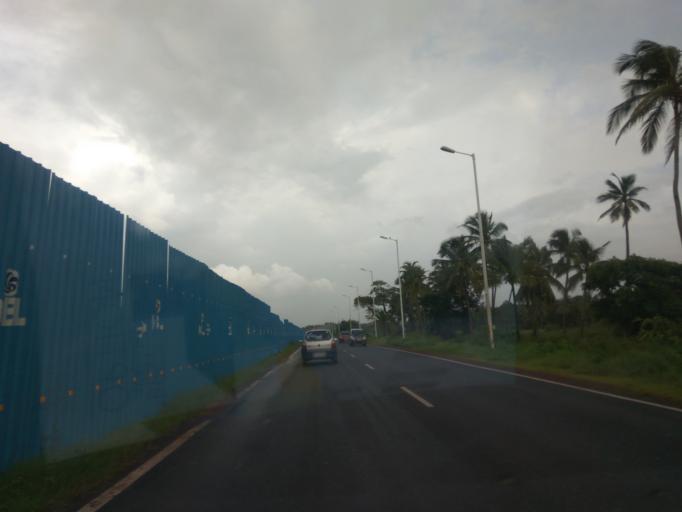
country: IN
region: Goa
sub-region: North Goa
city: Goa Velha
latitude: 15.4320
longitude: 73.8878
